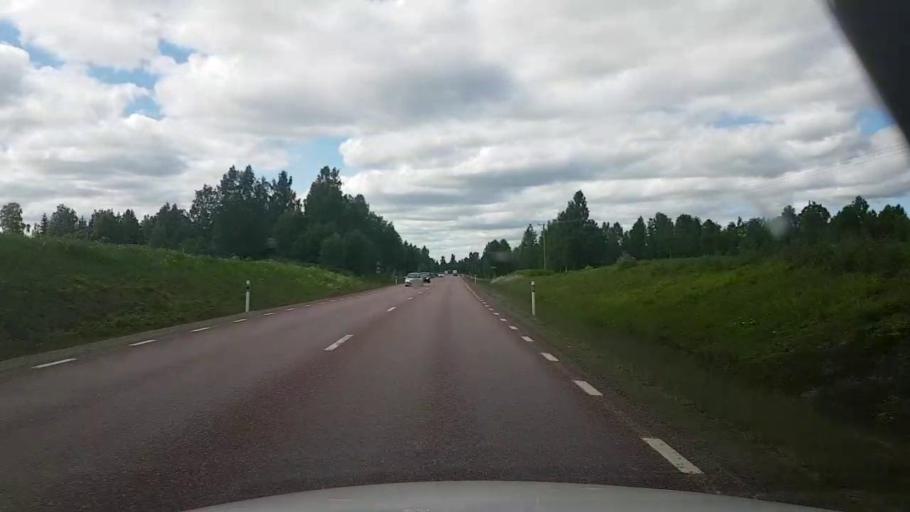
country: SE
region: Gaevleborg
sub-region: Ljusdals Kommun
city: Ljusdal
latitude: 61.8097
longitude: 16.0939
